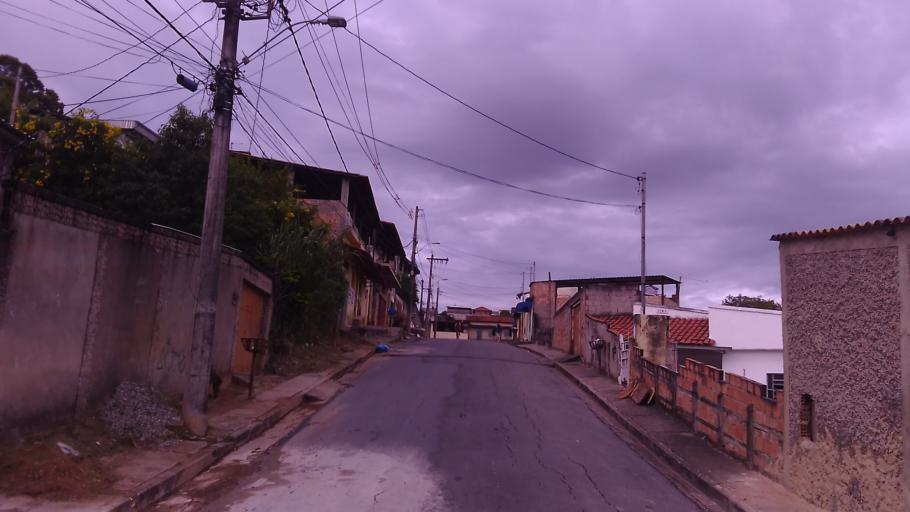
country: BR
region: Minas Gerais
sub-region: Contagem
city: Contagem
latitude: -19.9164
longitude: -44.0196
